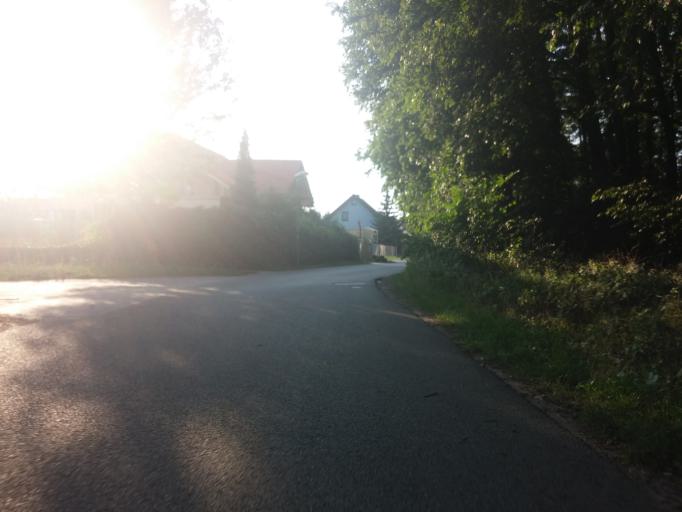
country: CZ
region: Central Bohemia
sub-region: Okres Nymburk
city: Podebrady
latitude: 50.1330
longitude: 15.1103
